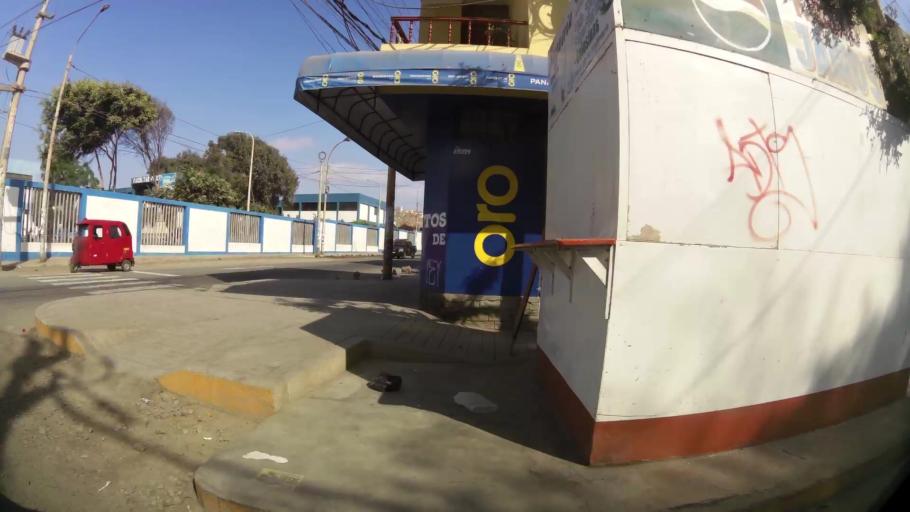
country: PE
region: Lima
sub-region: Huaura
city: Huacho
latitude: -11.1237
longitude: -77.6105
